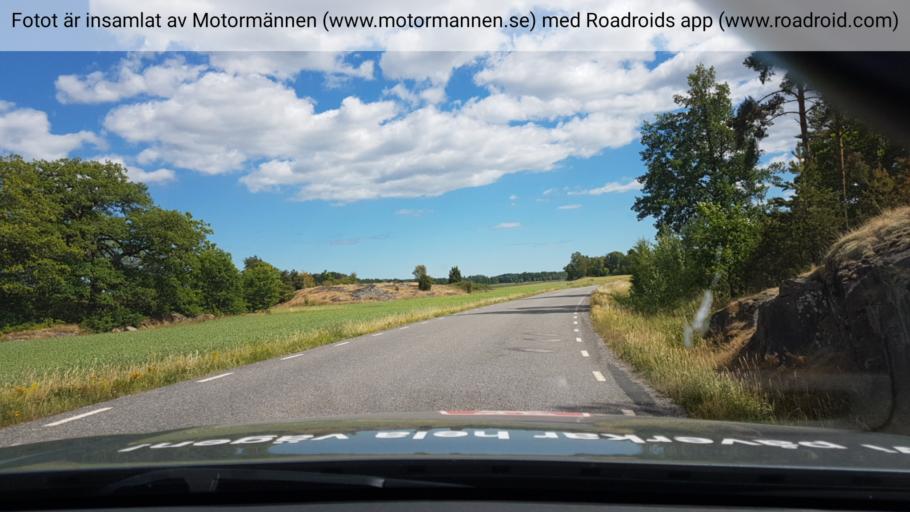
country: SE
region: Kalmar
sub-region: Vasterviks Kommun
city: Forserum
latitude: 58.0062
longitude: 16.5845
